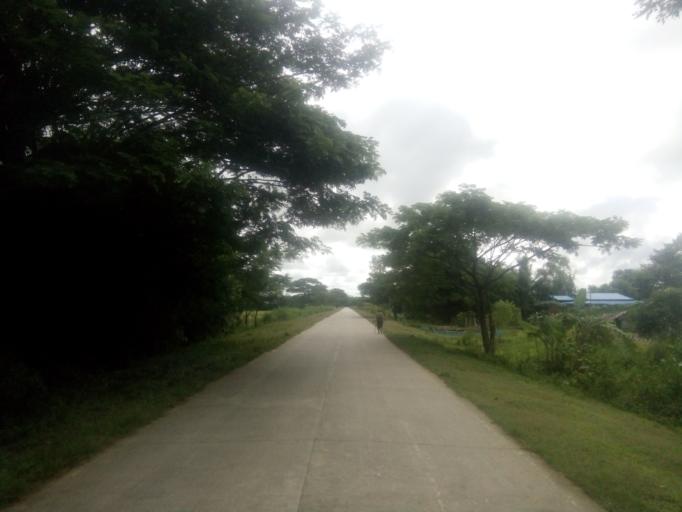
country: MM
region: Bago
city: Nyaunglebin
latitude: 17.9209
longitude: 96.5183
